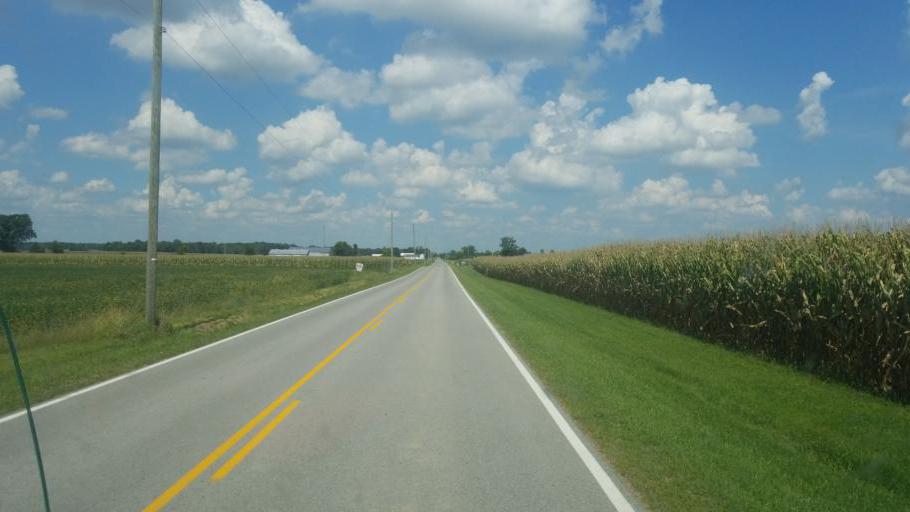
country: US
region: Ohio
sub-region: Hancock County
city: Arlington
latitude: 40.8745
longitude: -83.7272
